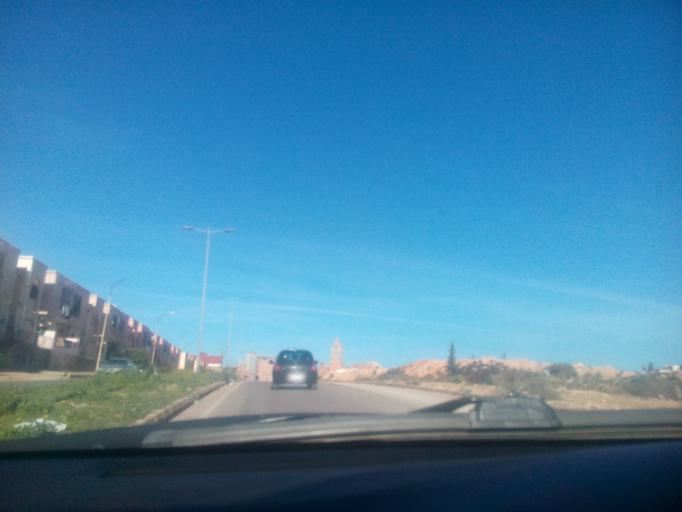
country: DZ
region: Oran
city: Bir el Djir
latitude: 35.7471
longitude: -0.5499
